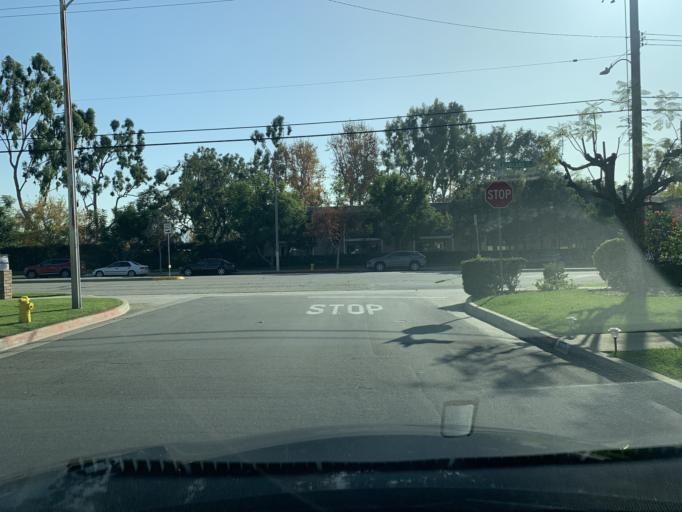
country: US
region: California
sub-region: Los Angeles County
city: Covina
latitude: 34.0794
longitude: -117.8929
